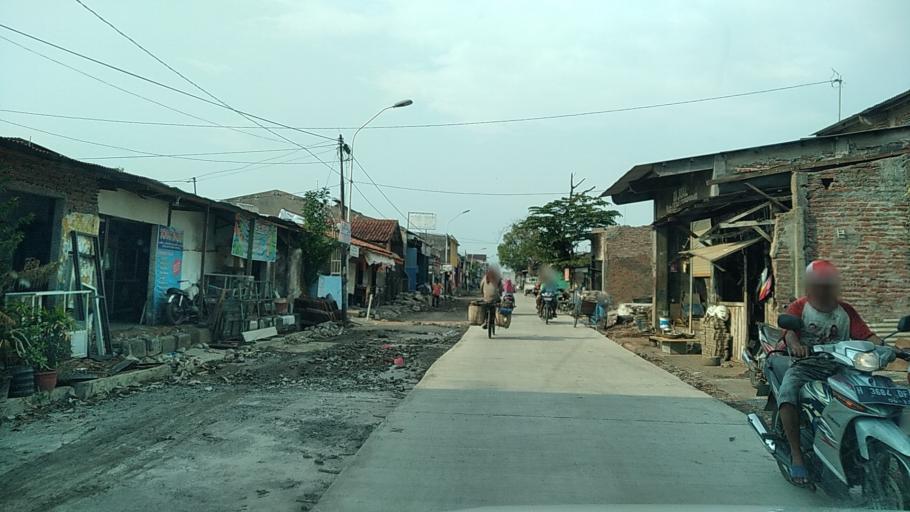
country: ID
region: Central Java
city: Semarang
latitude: -6.9764
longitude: 110.4416
